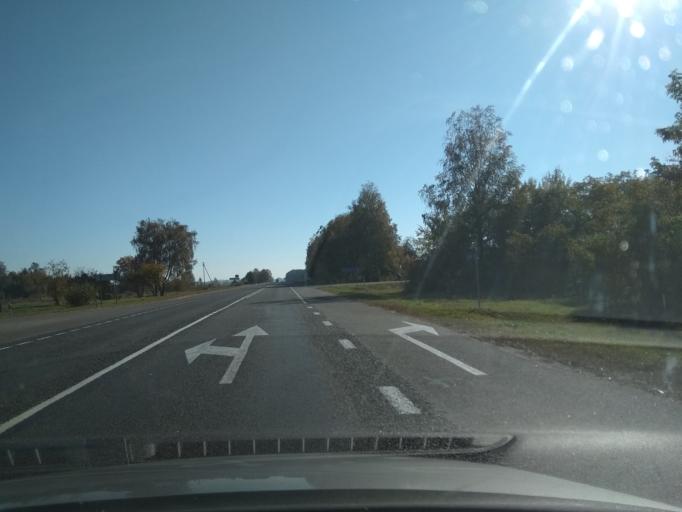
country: BY
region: Brest
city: Malaryta
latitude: 51.9502
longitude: 24.0098
